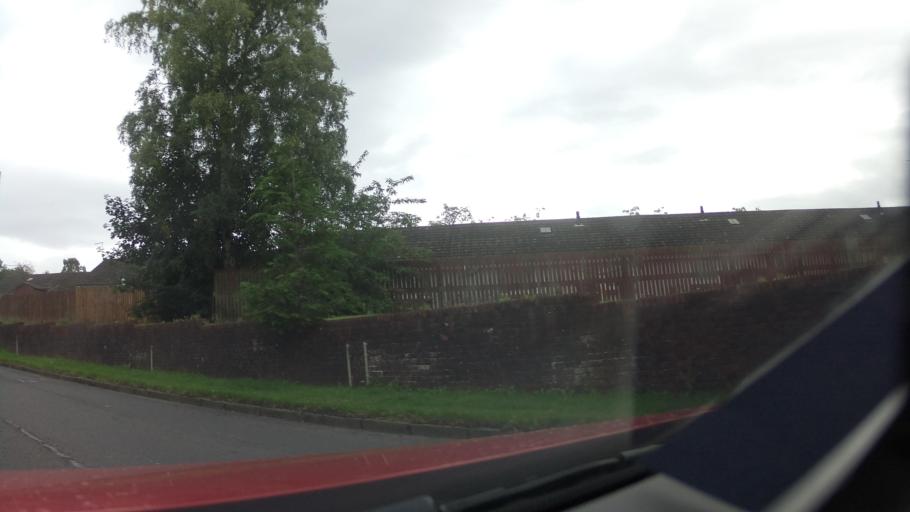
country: GB
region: Scotland
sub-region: Clackmannanshire
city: Clackmannan
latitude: 56.1105
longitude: -3.7565
